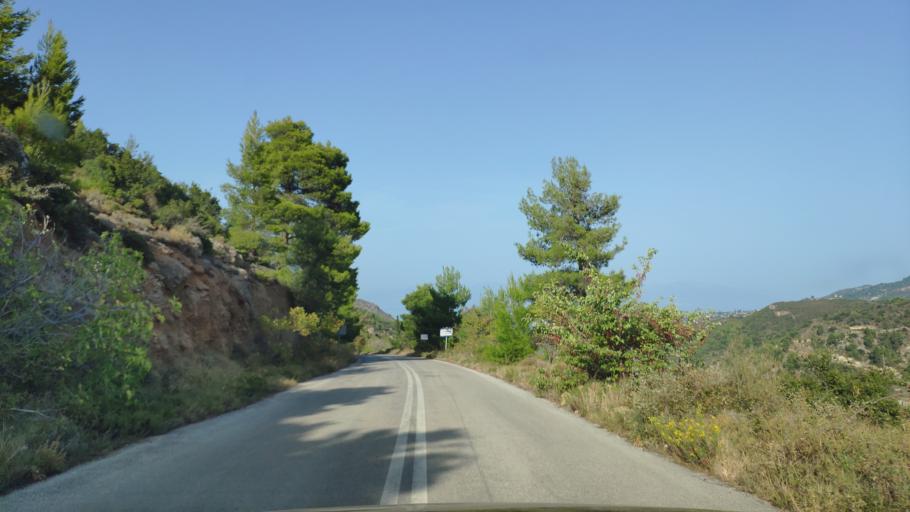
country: GR
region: West Greece
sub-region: Nomos Achaias
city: Aiyira
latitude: 38.0695
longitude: 22.3918
